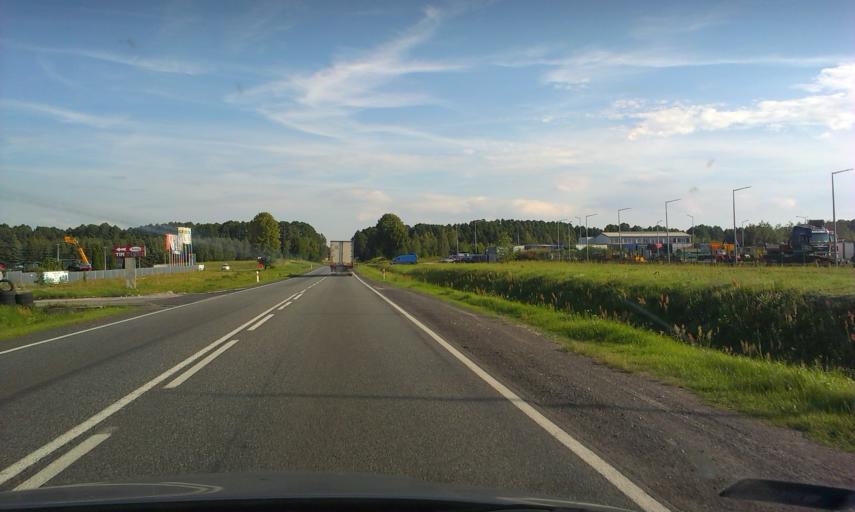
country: PL
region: Kujawsko-Pomorskie
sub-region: Powiat bydgoski
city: Biale Blota
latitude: 53.1327
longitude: 17.8799
